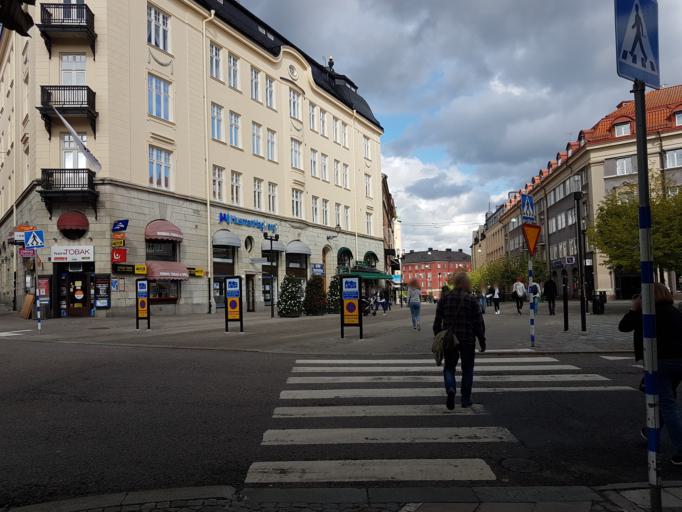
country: SE
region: Stockholm
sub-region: Sodertalje Kommun
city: Soedertaelje
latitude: 59.1933
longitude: 17.6270
